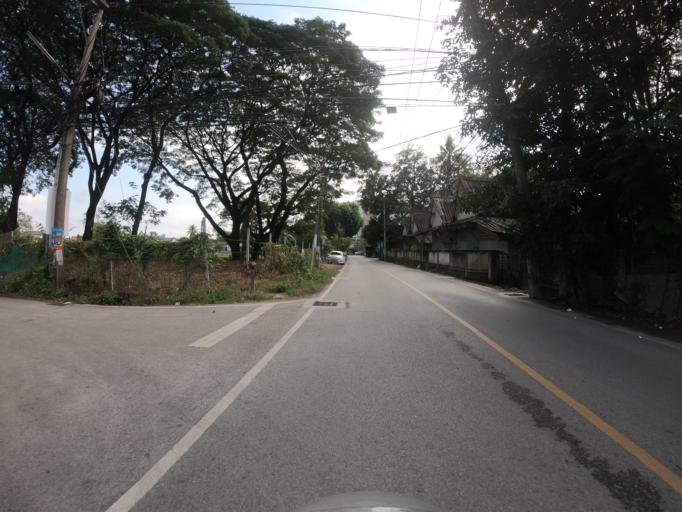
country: TH
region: Chiang Mai
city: Chiang Mai
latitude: 18.8059
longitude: 98.9678
